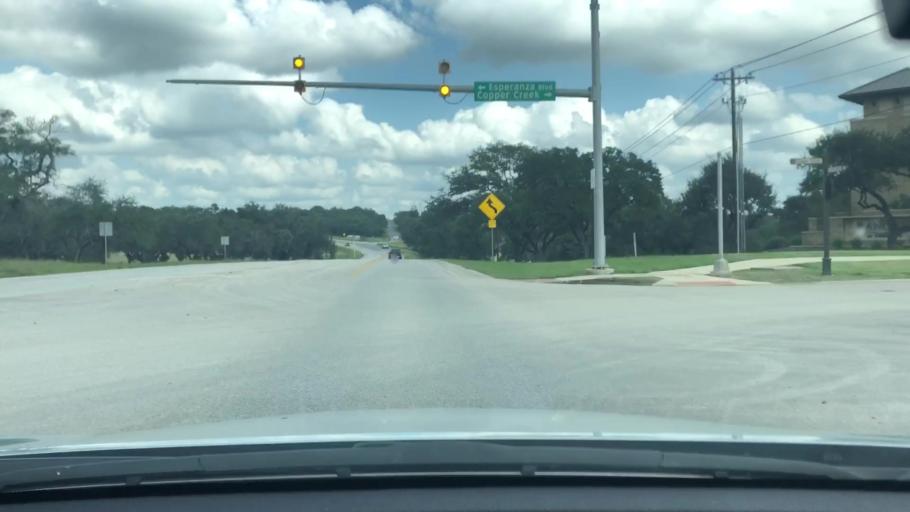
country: US
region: Texas
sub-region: Kendall County
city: Boerne
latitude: 29.7871
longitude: -98.6933
